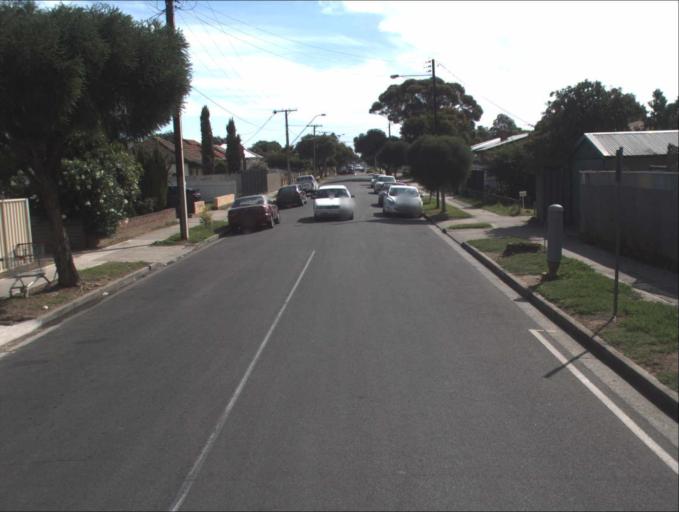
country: AU
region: South Australia
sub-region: Port Adelaide Enfield
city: Blair Athol
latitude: -34.8595
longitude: 138.5920
